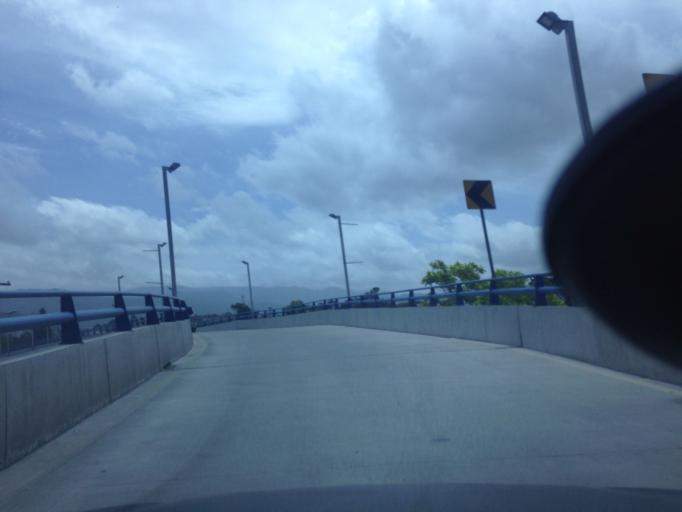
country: HN
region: Francisco Morazan
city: Tegucigalpa
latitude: 14.0697
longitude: -87.2147
